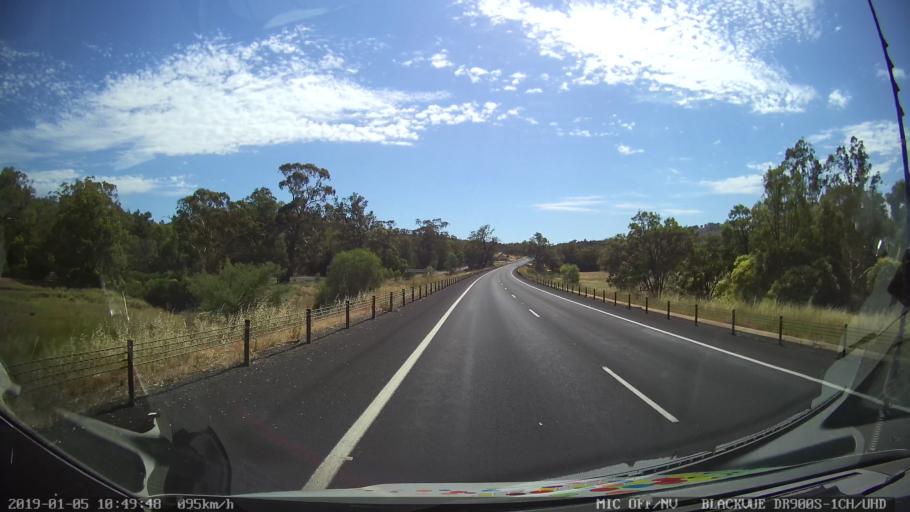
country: AU
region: New South Wales
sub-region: Warrumbungle Shire
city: Coonabarabran
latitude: -31.4316
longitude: 149.0658
